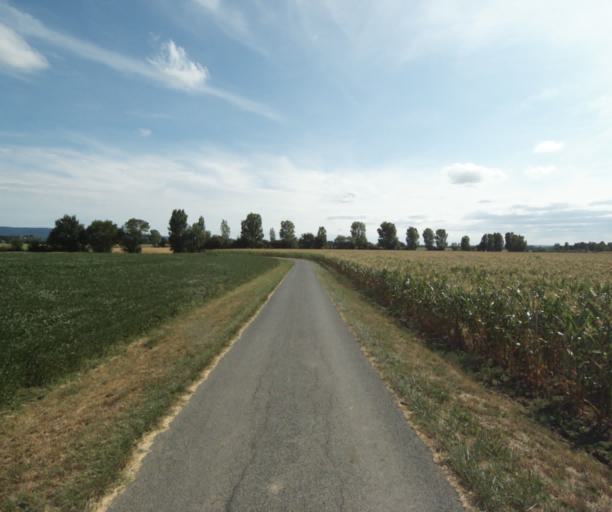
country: FR
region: Midi-Pyrenees
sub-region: Departement du Tarn
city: Puylaurens
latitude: 43.5195
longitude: 1.9848
